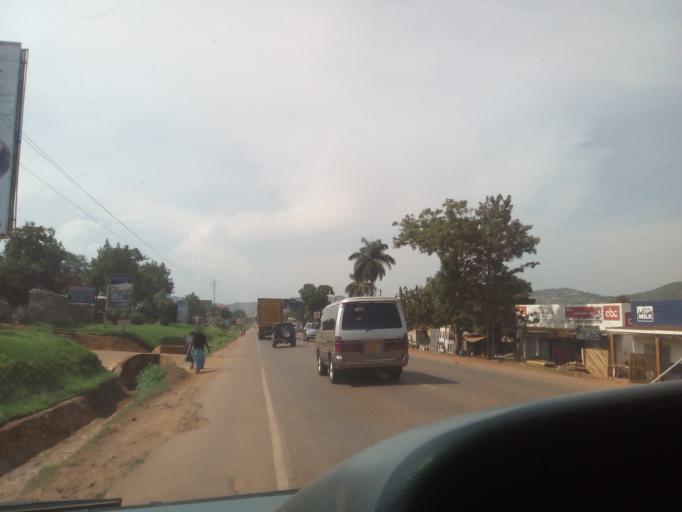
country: UG
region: Central Region
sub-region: Wakiso District
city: Kajansi
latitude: 0.1972
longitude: 32.5397
